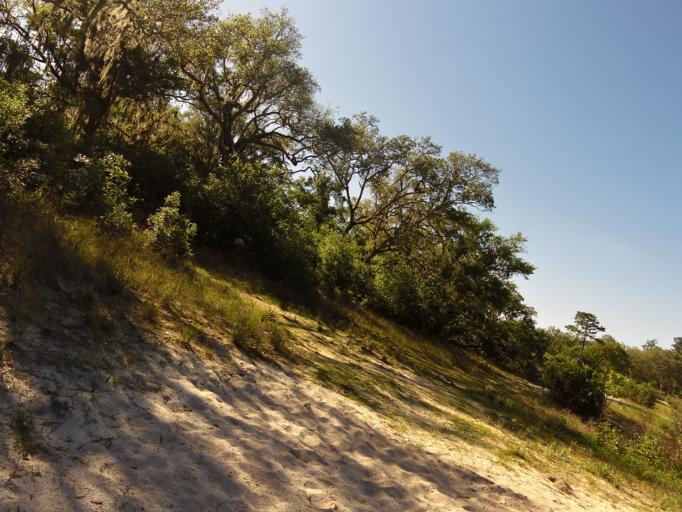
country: US
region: Florida
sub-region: Clay County
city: Keystone Heights
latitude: 29.8207
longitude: -81.9442
